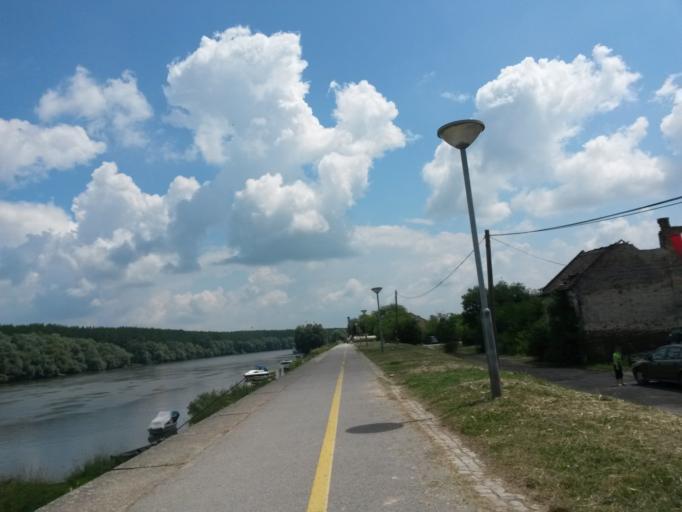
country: HR
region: Osjecko-Baranjska
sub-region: Grad Osijek
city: Osijek
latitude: 45.5616
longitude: 18.7243
